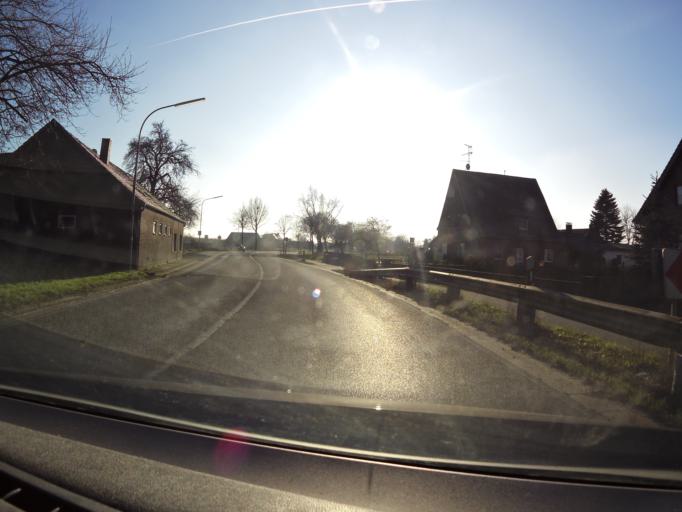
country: DE
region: North Rhine-Westphalia
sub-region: Regierungsbezirk Dusseldorf
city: Bruggen
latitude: 51.3001
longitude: 6.2004
